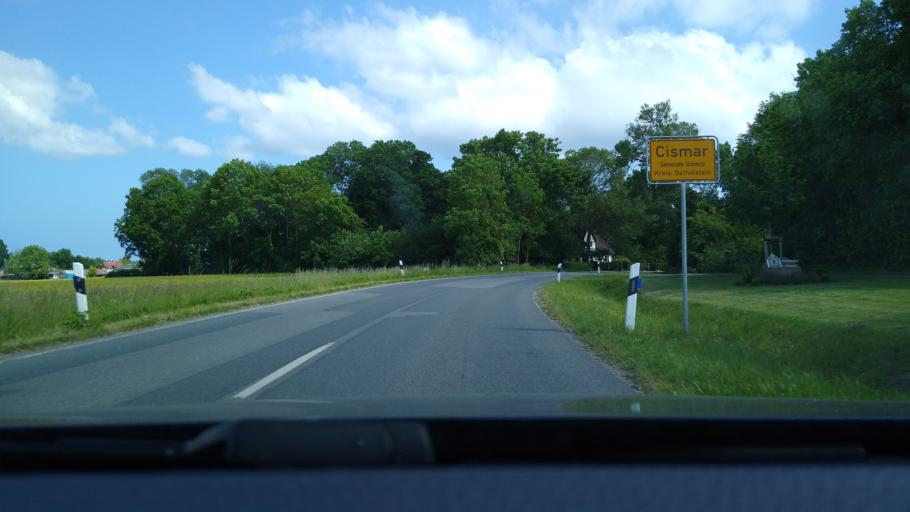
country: DE
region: Schleswig-Holstein
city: Riepsdorf
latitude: 54.1933
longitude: 10.9834
